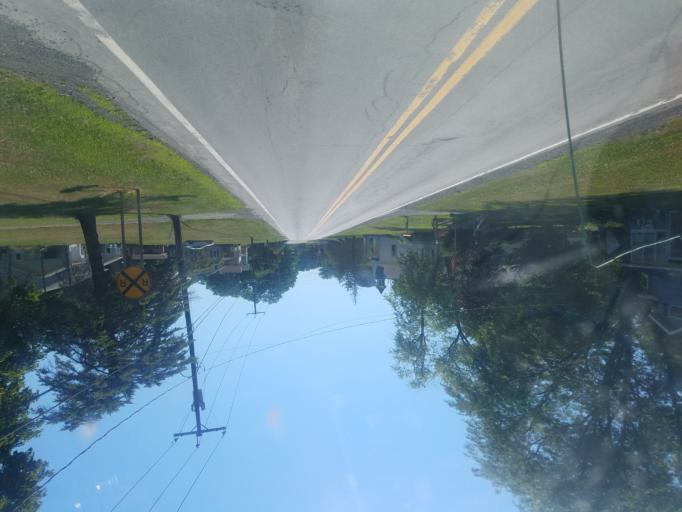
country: US
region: New York
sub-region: Ontario County
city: Phelps
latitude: 42.9325
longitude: -77.0093
